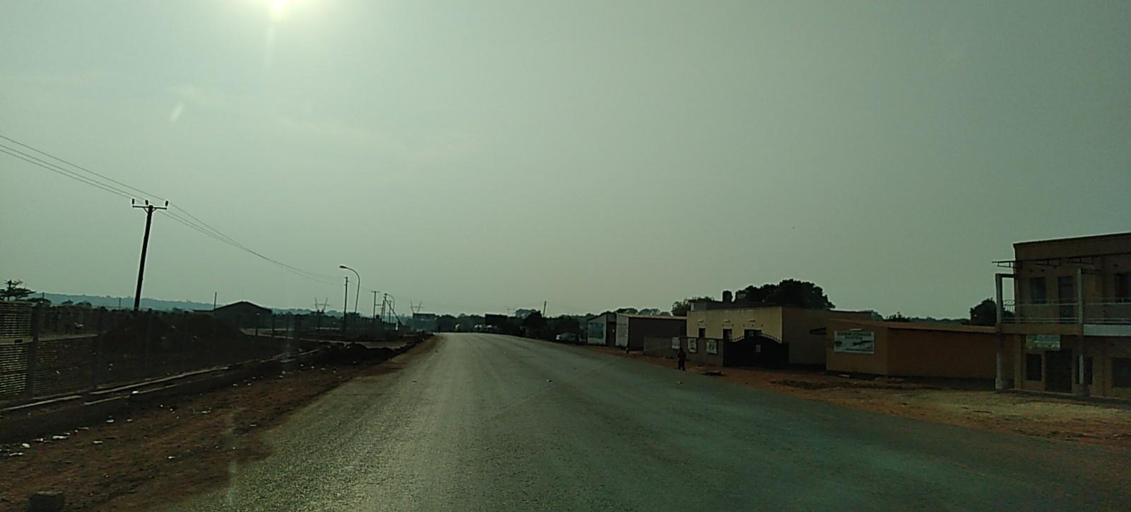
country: ZM
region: North-Western
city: Solwezi
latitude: -12.1929
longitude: 26.4461
